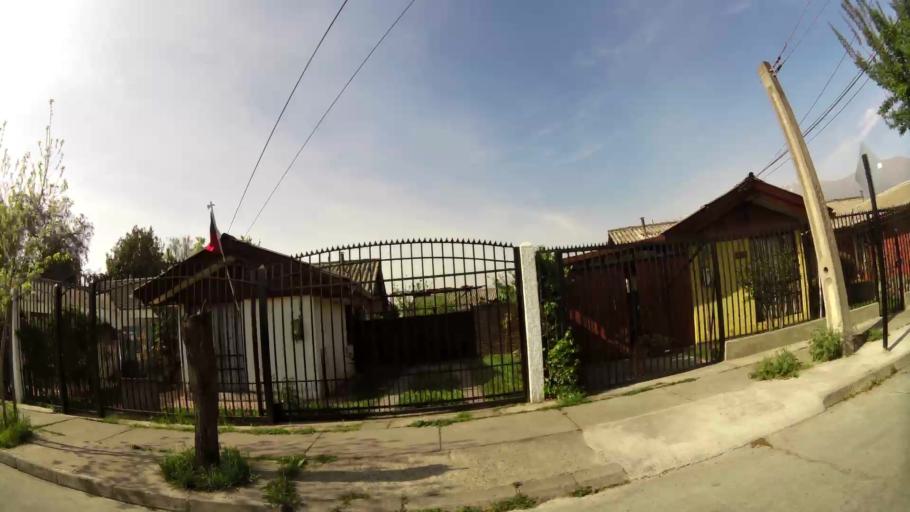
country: CL
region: Santiago Metropolitan
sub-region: Provincia de Santiago
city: Villa Presidente Frei, Nunoa, Santiago, Chile
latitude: -33.5162
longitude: -70.5918
